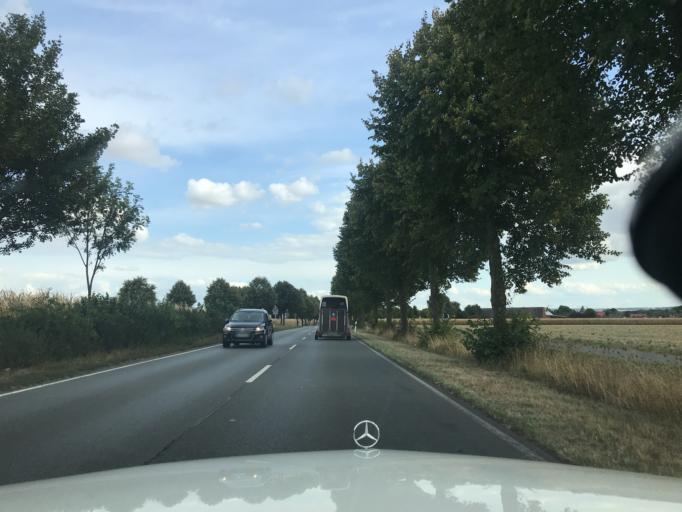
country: DE
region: North Rhine-Westphalia
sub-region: Regierungsbezirk Arnsberg
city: Lippstadt
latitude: 51.6442
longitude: 8.3854
